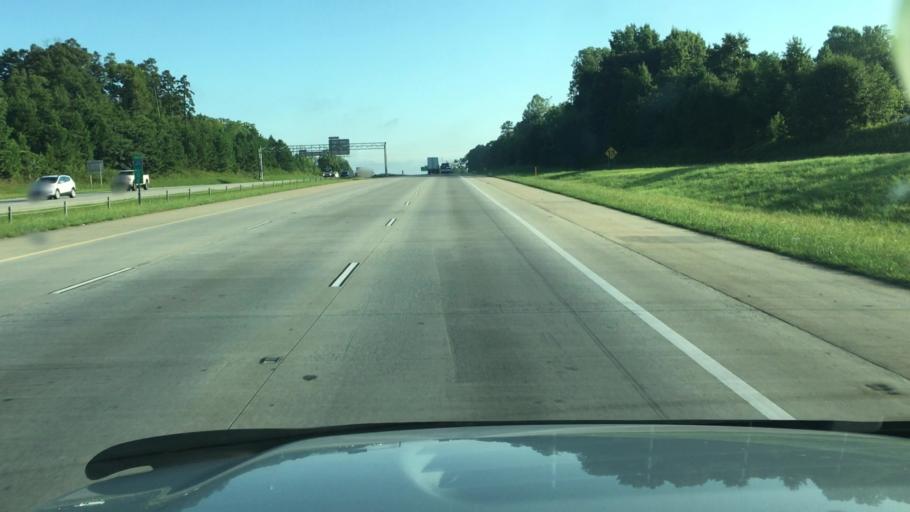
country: US
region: North Carolina
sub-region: Gaston County
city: Mount Holly
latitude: 35.2755
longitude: -80.9659
